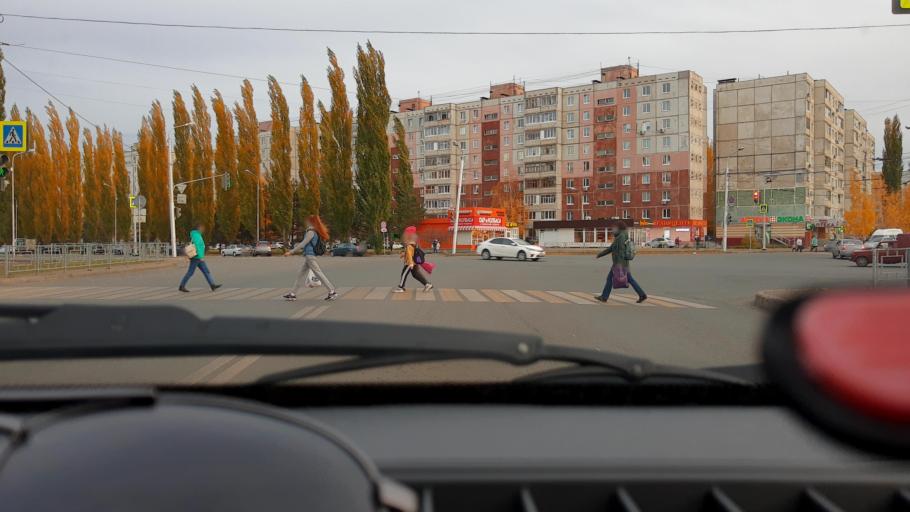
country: RU
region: Bashkortostan
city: Ufa
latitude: 54.7741
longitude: 56.0788
